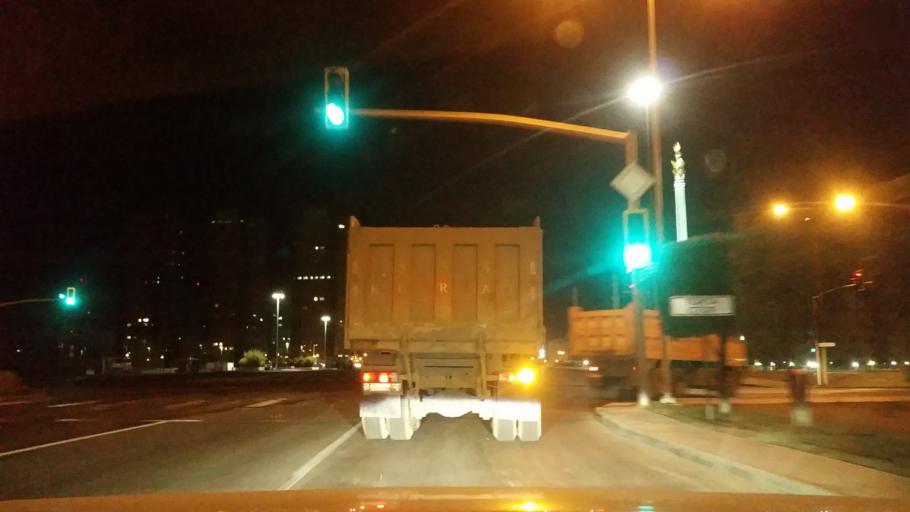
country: KZ
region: Astana Qalasy
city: Astana
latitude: 51.1197
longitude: 71.4674
